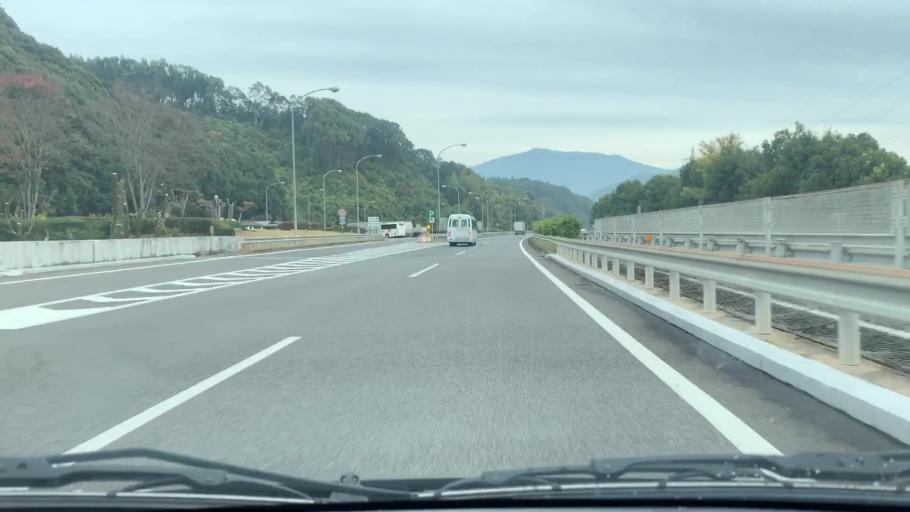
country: JP
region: Saga Prefecture
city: Takeocho-takeo
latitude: 33.2608
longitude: 130.0823
